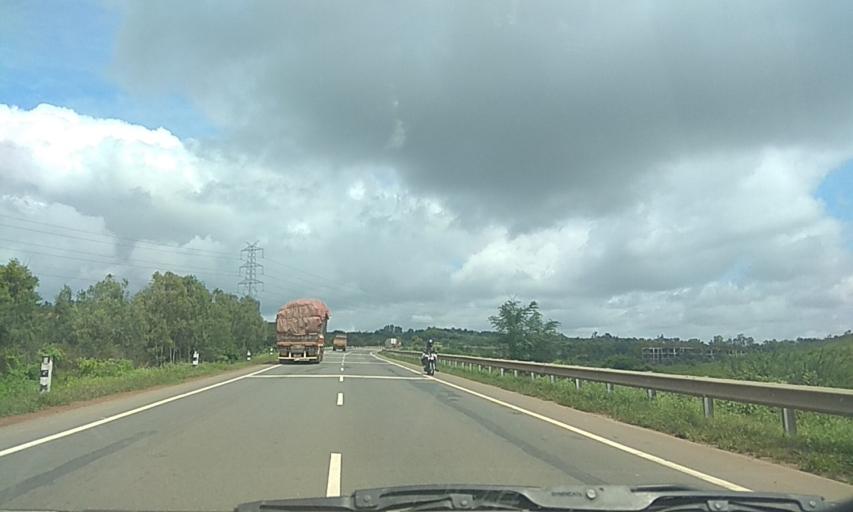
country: IN
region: Karnataka
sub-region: Dharwad
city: Hubli
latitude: 15.4296
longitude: 74.9675
